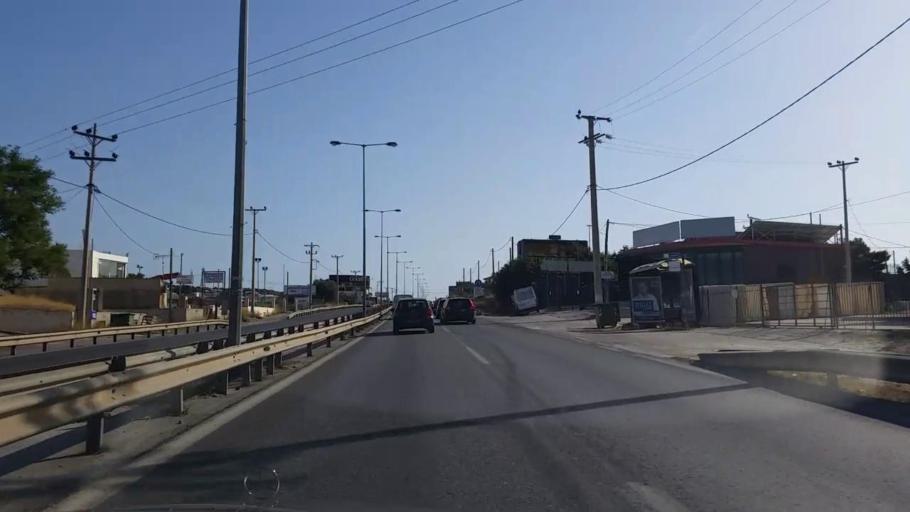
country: GR
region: Attica
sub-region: Nomarchia Anatolikis Attikis
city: Kitsi
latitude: 37.8666
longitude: 23.8520
